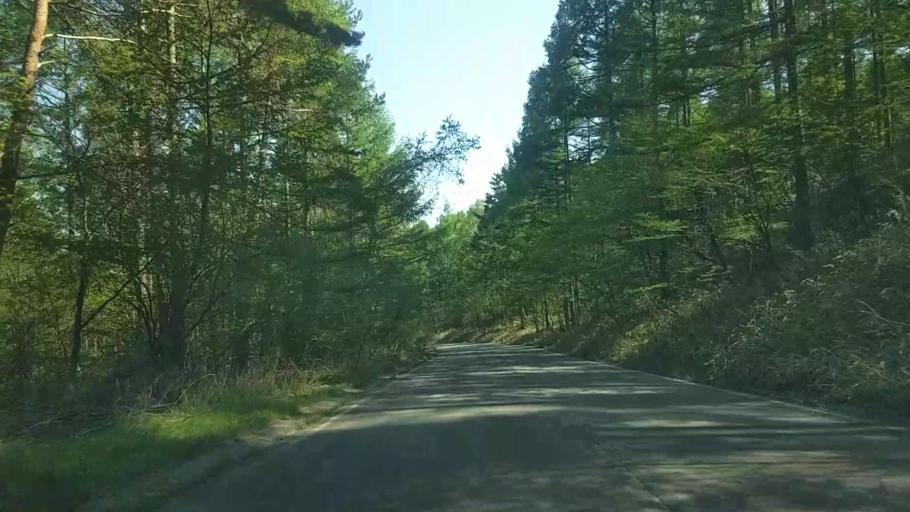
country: JP
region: Yamanashi
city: Nirasaki
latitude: 35.9203
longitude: 138.4026
